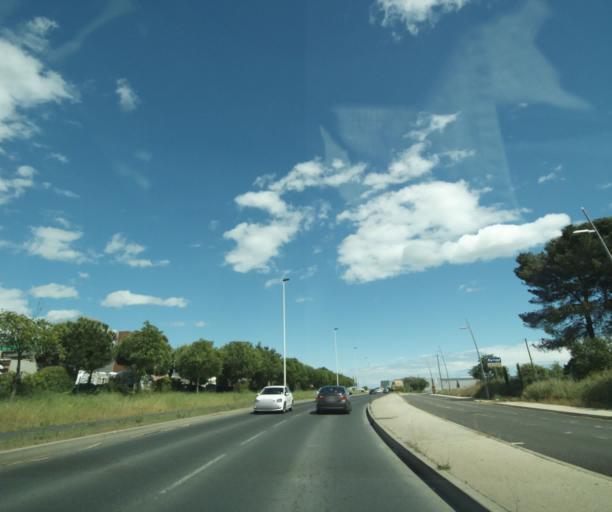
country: FR
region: Languedoc-Roussillon
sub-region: Departement de l'Herault
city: Saint-Jean-de-Vedas
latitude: 43.5752
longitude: 3.8638
